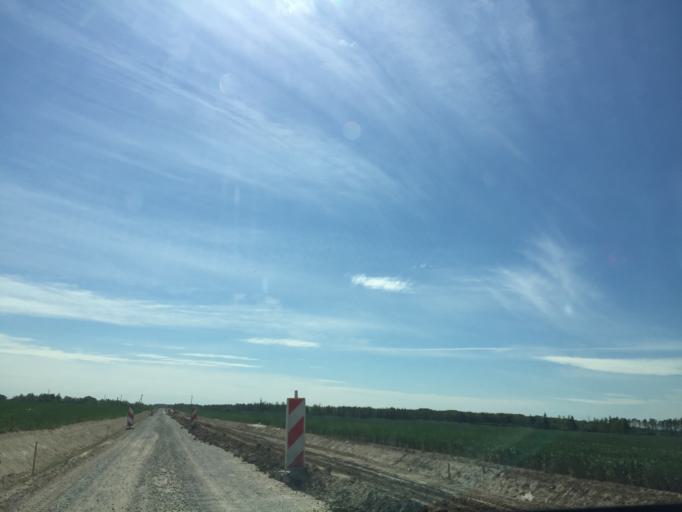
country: LT
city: Linkuva
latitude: 56.0582
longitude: 24.0870
